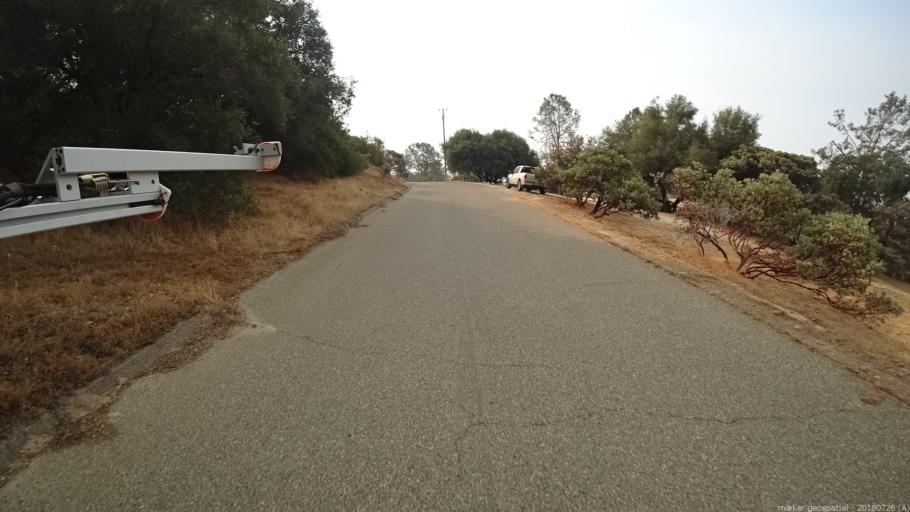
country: US
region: California
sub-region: Madera County
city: Coarsegold
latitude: 37.2252
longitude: -119.7192
